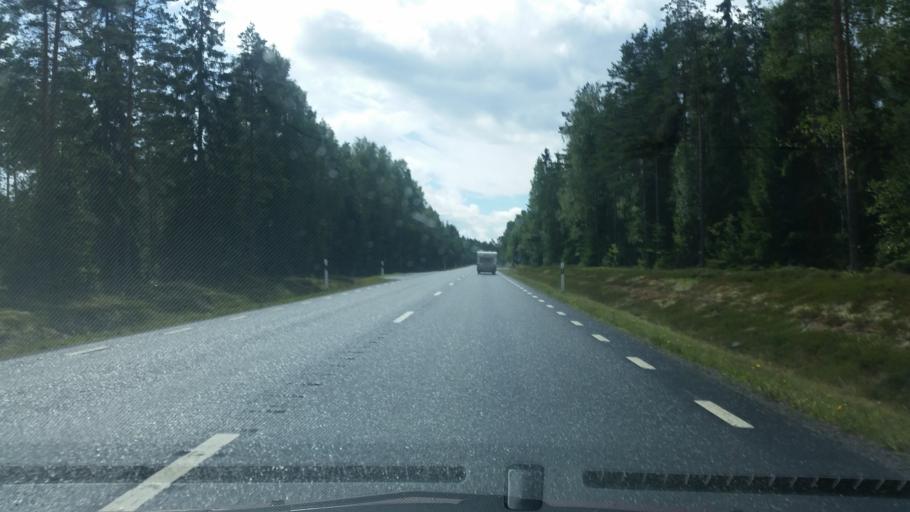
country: SE
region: Joenkoeping
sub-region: Gislaveds Kommun
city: Gislaved
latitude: 57.3931
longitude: 13.5907
